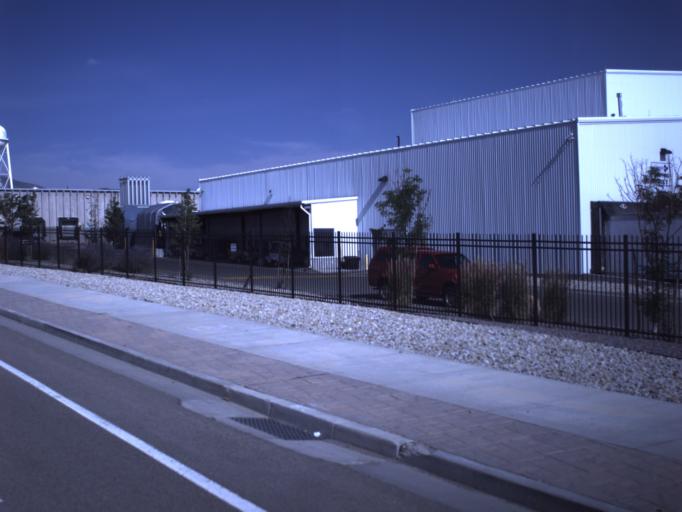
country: US
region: Utah
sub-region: Salt Lake County
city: Oquirrh
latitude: 40.6533
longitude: -112.0461
